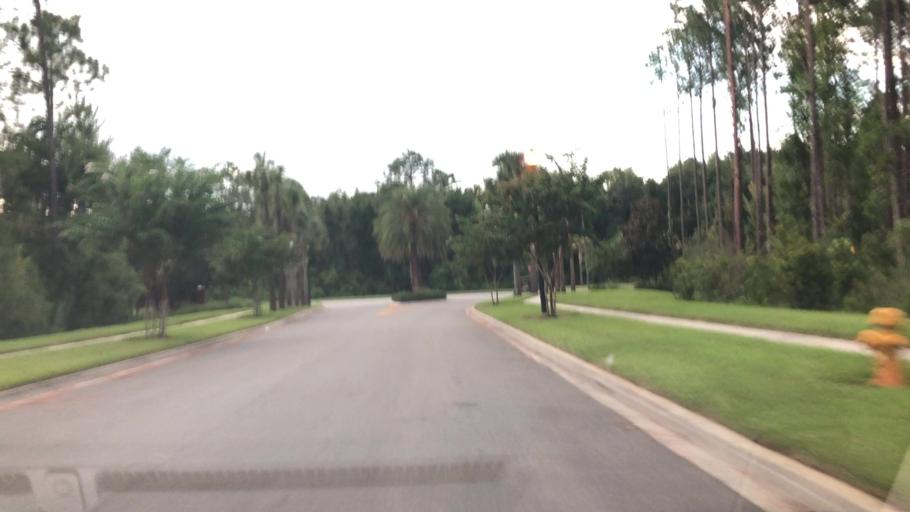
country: US
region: Florida
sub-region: Saint Johns County
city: Palm Valley
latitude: 30.1210
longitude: -81.4458
